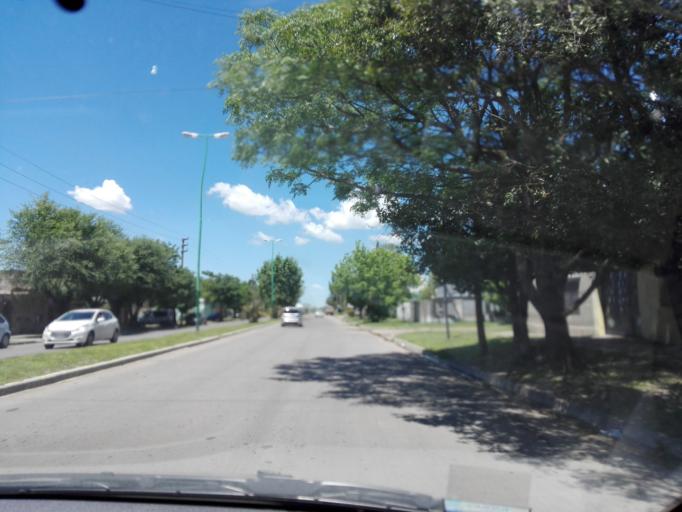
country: AR
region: Buenos Aires
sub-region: Partido de La Plata
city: La Plata
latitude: -34.9004
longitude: -58.0104
